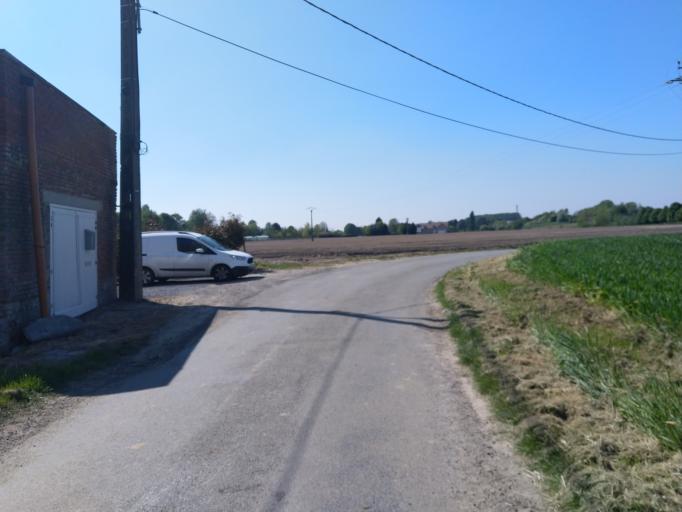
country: BE
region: Wallonia
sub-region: Province du Hainaut
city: Jurbise
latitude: 50.5345
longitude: 3.9741
